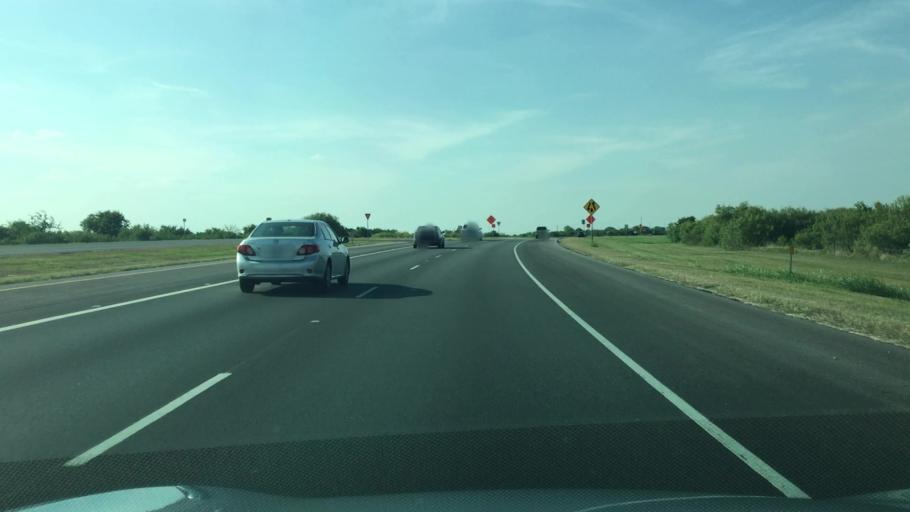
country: US
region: Texas
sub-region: Hays County
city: Buda
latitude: 30.0433
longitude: -97.8745
